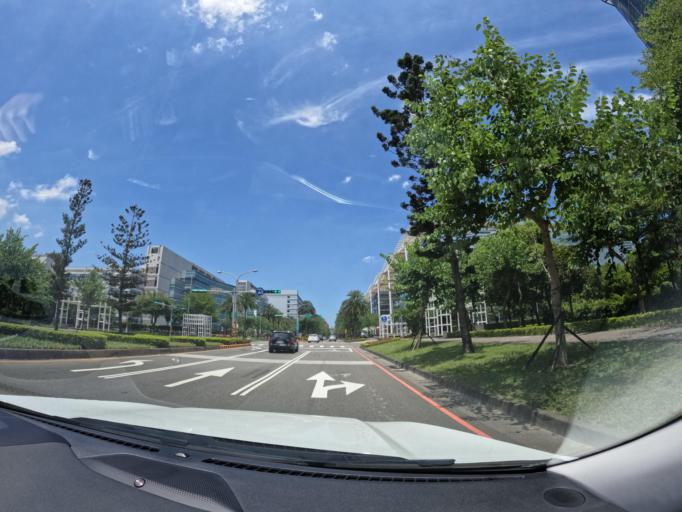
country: TW
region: Taiwan
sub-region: Taoyuan
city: Taoyuan
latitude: 25.0481
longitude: 121.3761
